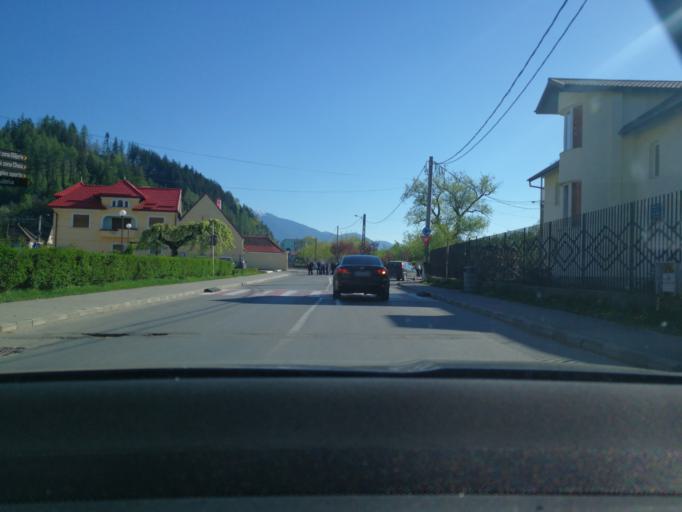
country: RO
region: Brasov
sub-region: Oras Rasnov
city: Rasnov
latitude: 45.5836
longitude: 25.4613
